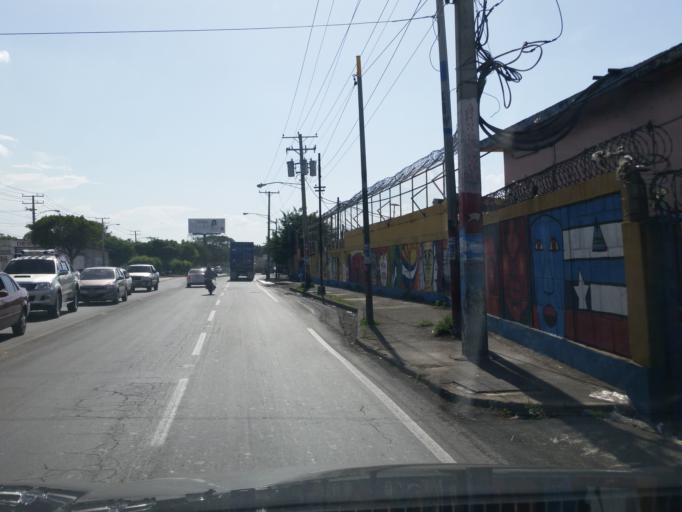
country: NI
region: Managua
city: Managua
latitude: 12.1538
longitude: -86.2602
